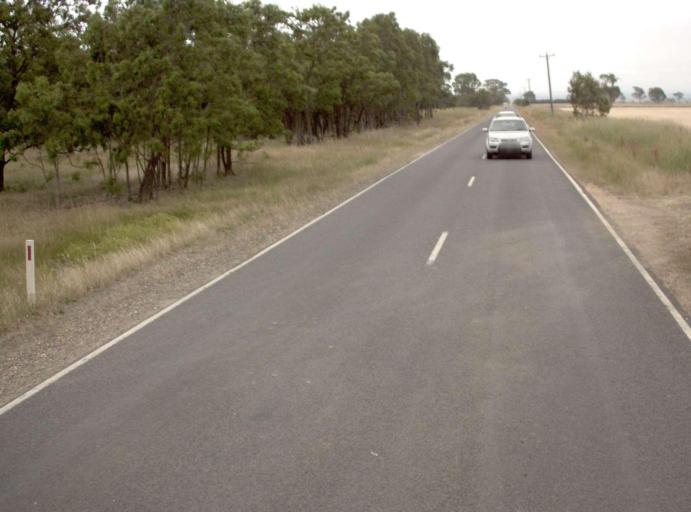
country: AU
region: Victoria
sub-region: Wellington
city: Heyfield
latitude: -38.0482
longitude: 146.7678
